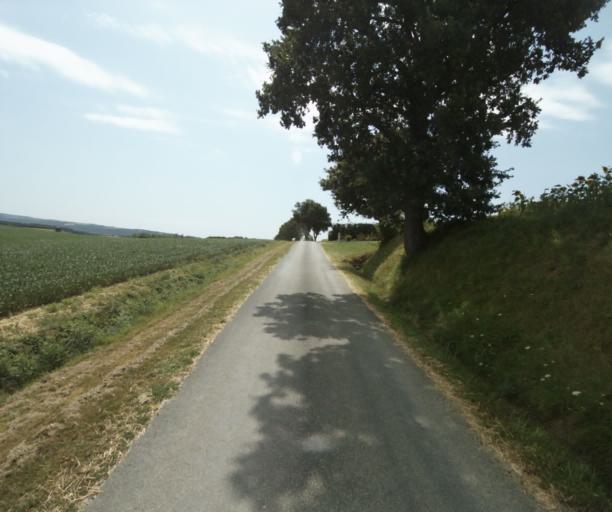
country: FR
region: Midi-Pyrenees
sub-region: Departement de la Haute-Garonne
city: Saint-Felix-Lauragais
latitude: 43.4269
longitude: 1.9111
